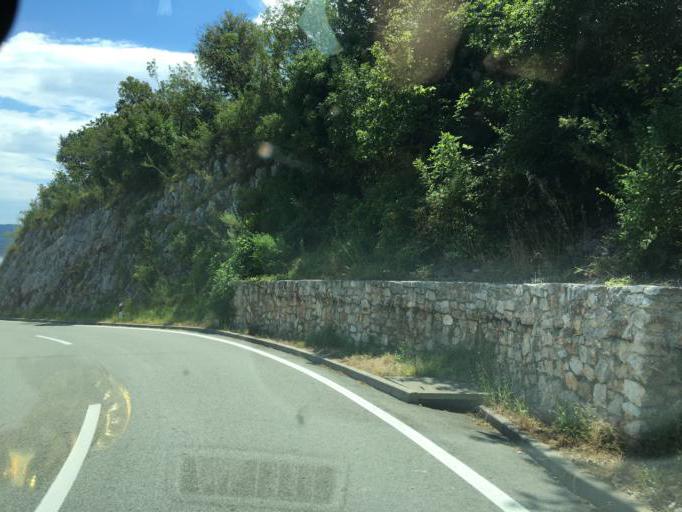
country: HR
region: Istarska
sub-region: Grad Labin
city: Rabac
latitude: 45.1453
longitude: 14.2197
